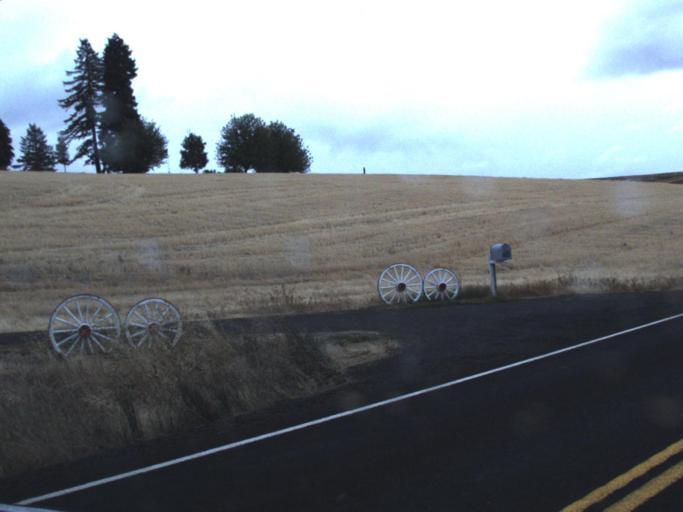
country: US
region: Washington
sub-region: Whitman County
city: Colfax
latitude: 47.1371
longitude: -117.2451
